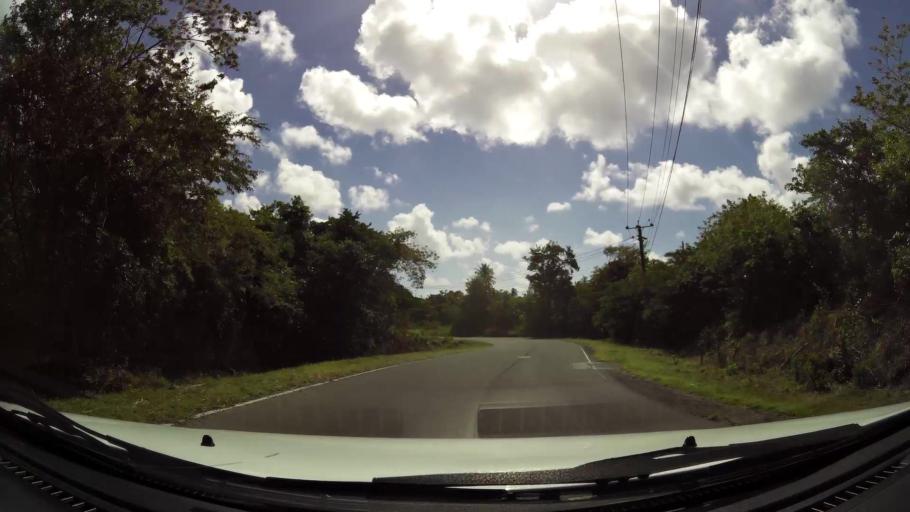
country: LC
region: Laborie Quarter
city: Laborie
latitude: 13.7545
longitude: -61.0089
